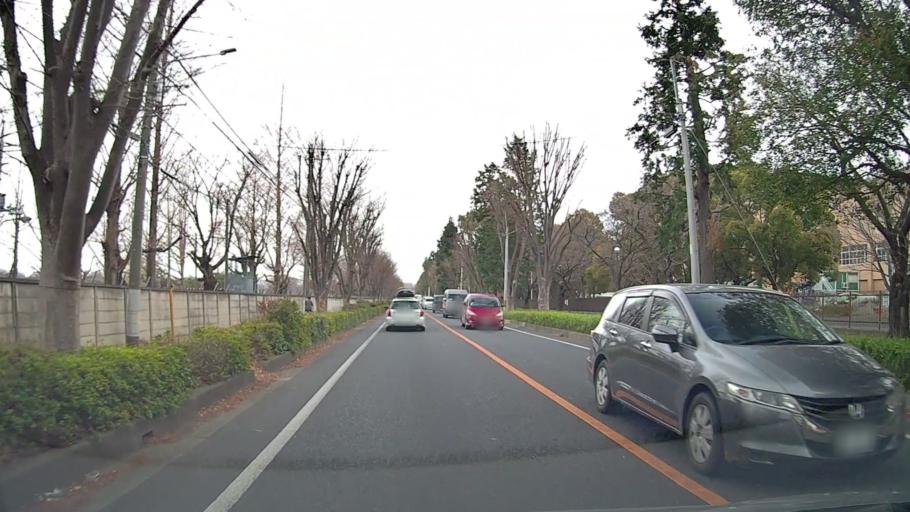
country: JP
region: Saitama
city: Asaka
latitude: 35.7833
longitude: 139.5906
